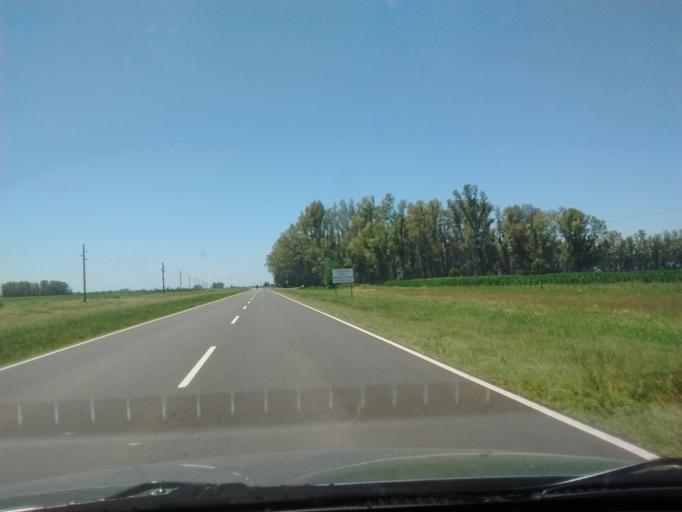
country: AR
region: Entre Rios
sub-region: Departamento de Gualeguay
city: Gualeguay
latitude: -33.0029
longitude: -59.5059
